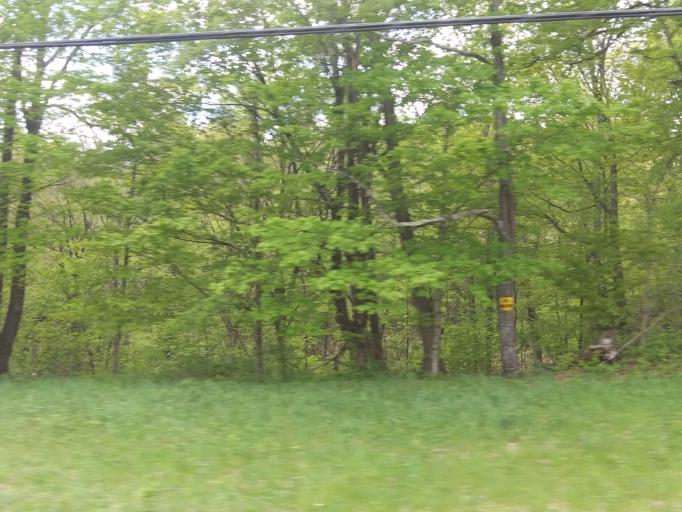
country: US
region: Massachusetts
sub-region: Franklin County
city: Buckland
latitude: 42.5796
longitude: -72.8146
